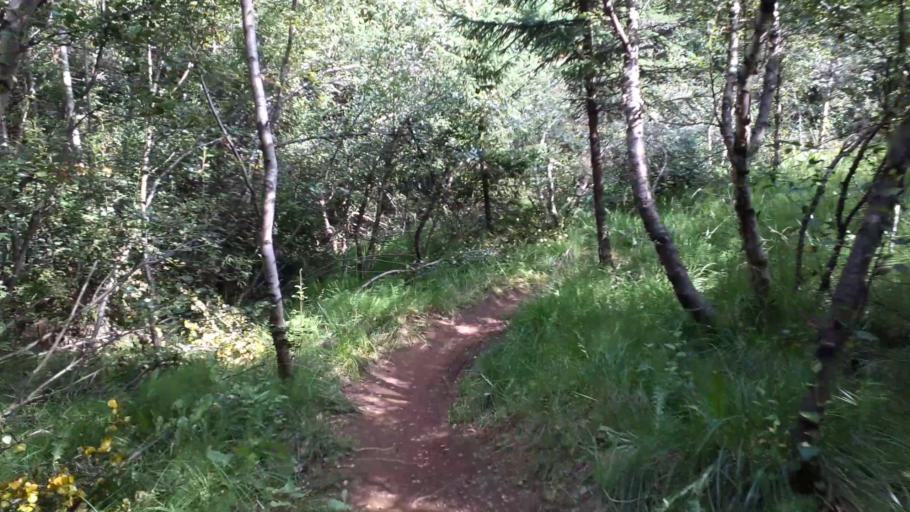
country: IS
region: Northeast
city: Akureyri
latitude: 65.6416
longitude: -18.0848
